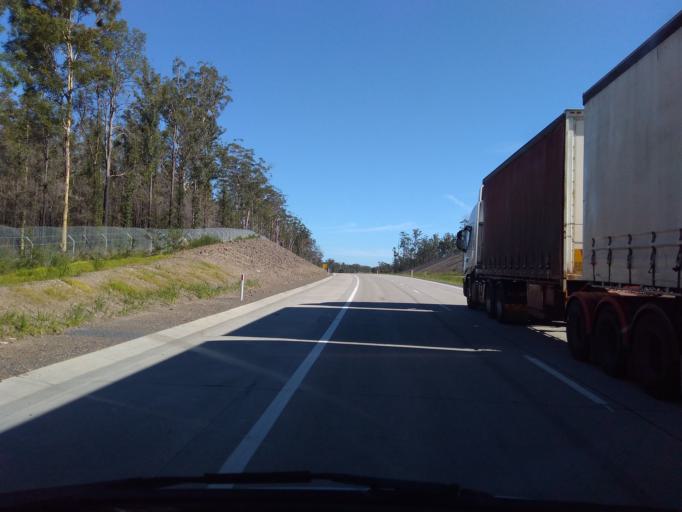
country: AU
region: New South Wales
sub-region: Kempsey
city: Kempsey
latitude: -31.1576
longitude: 152.8222
